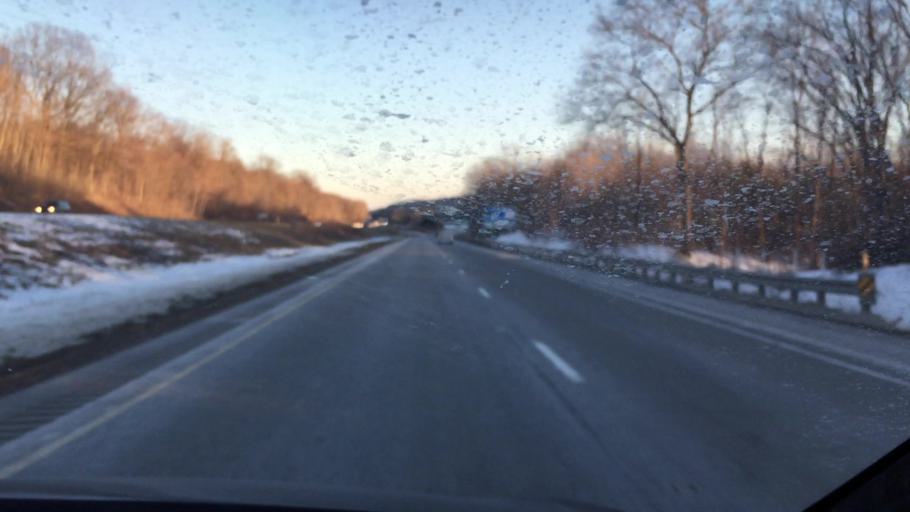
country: US
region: Pennsylvania
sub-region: Crawford County
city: Meadville
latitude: 41.6350
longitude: -80.1948
